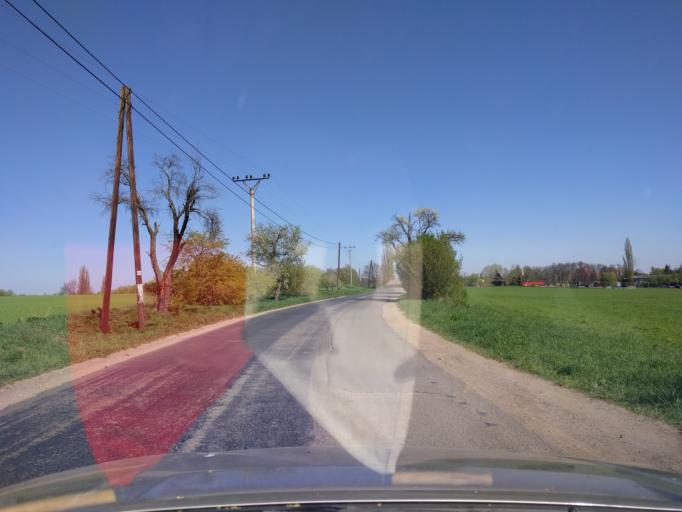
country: CZ
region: Central Bohemia
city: Cesky Brod
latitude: 50.0610
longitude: 14.8475
